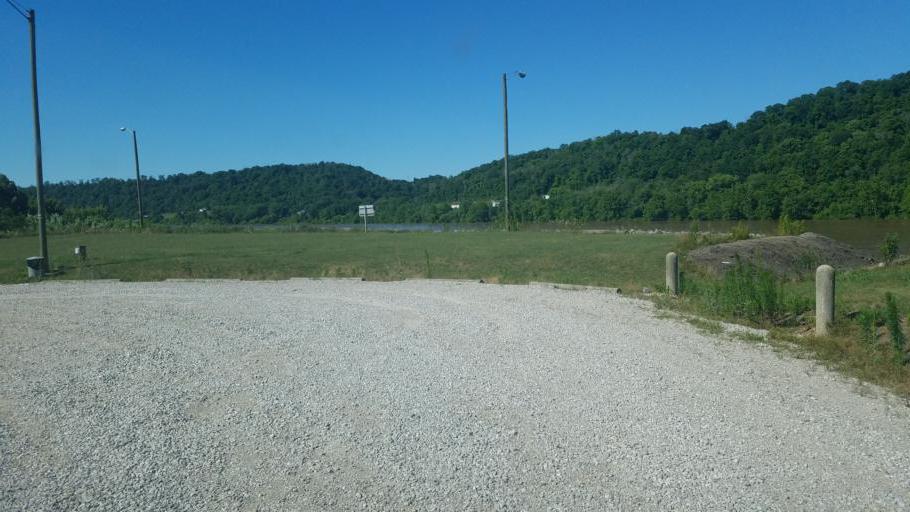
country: US
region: Ohio
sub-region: Gallia County
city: Gallipolis
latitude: 38.6703
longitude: -82.1835
